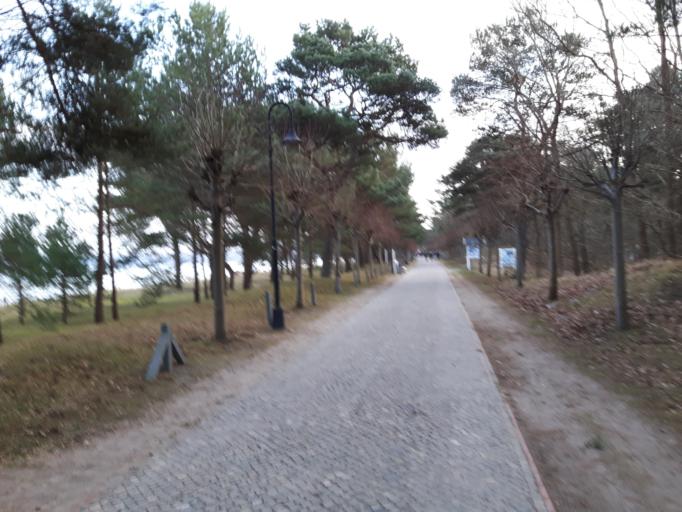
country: DE
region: Mecklenburg-Vorpommern
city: Ostseebad Binz
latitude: 54.4155
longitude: 13.5956
